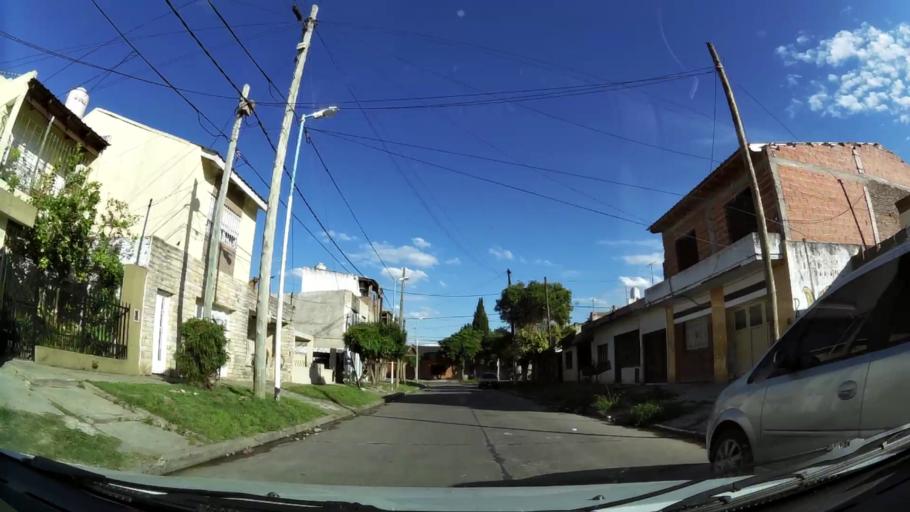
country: AR
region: Buenos Aires
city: Hurlingham
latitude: -34.5669
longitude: -58.6097
